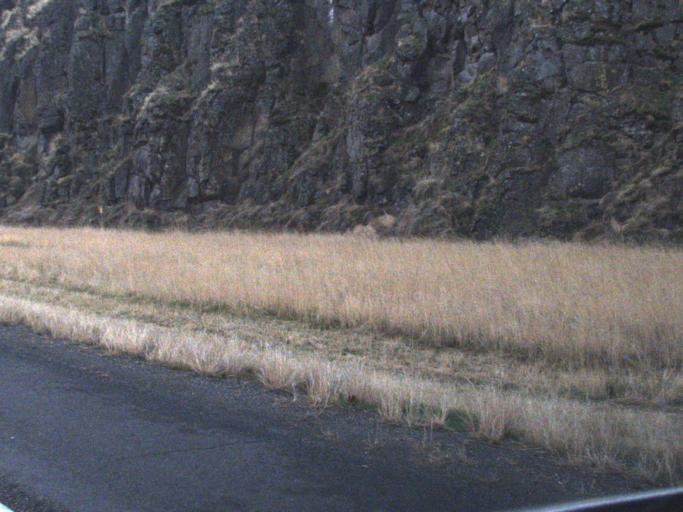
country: US
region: Washington
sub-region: Asotin County
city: Clarkston Heights-Vineland
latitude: 46.4174
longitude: -117.1041
